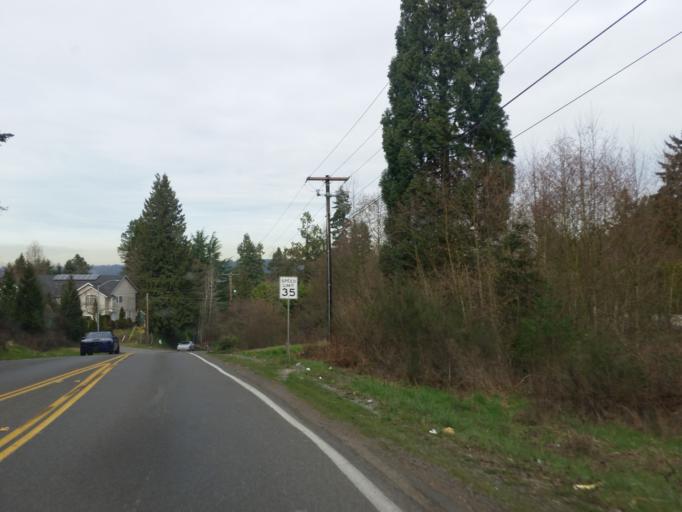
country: US
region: Washington
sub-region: Pierce County
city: Alderton
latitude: 47.1707
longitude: -122.2528
